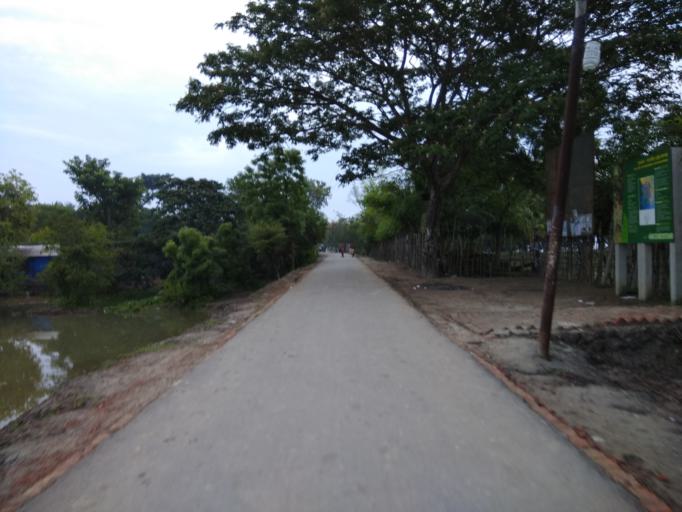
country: IN
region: West Bengal
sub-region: North 24 Parganas
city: Gosaba
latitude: 22.2484
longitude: 89.2397
